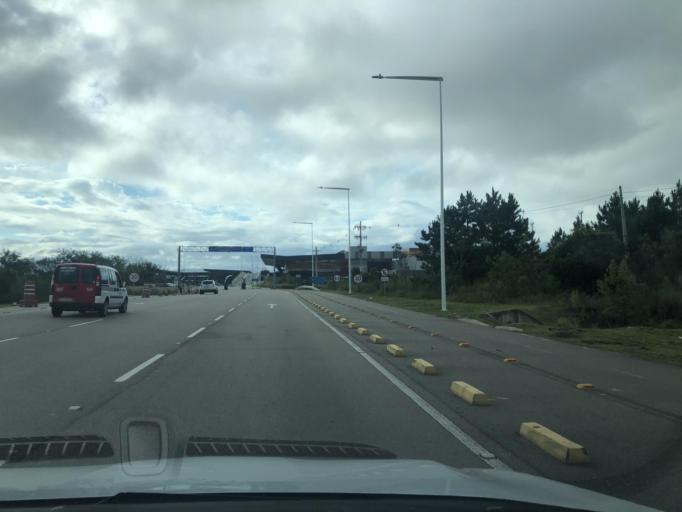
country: BR
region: Santa Catarina
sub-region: Florianopolis
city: Tapera
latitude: -27.6762
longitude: -48.5420
